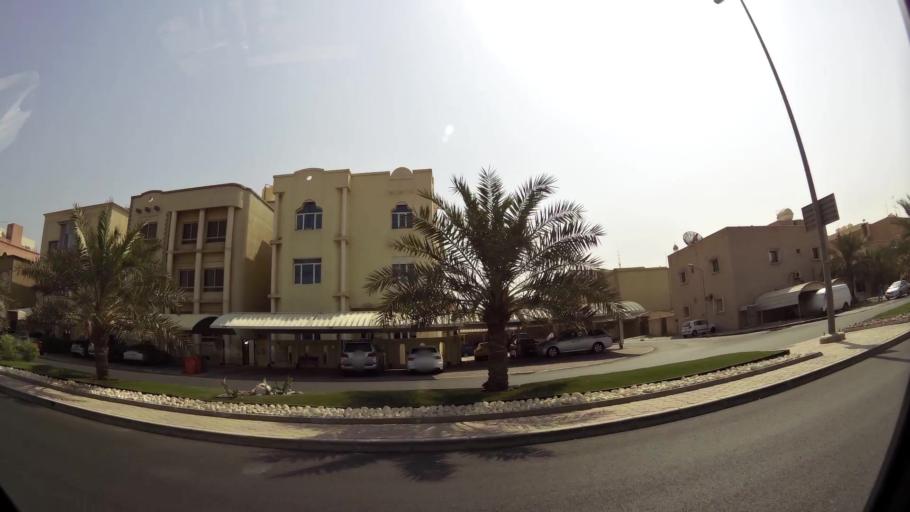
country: KW
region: Al Asimah
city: Ad Dasmah
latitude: 29.3447
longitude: 47.9997
